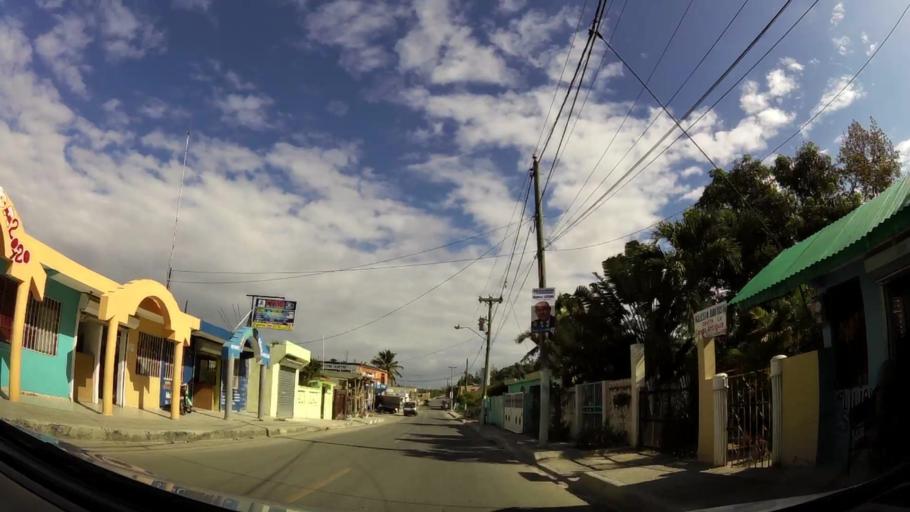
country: DO
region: Santo Domingo
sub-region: Santo Domingo
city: Boca Chica
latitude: 18.4616
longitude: -69.6052
